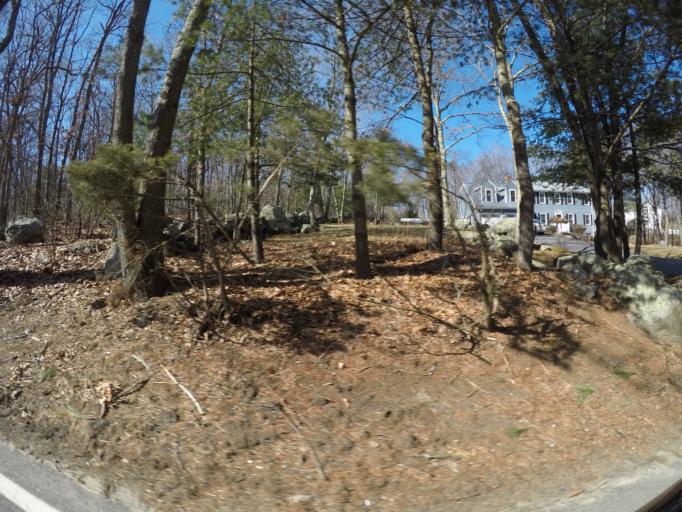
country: US
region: Massachusetts
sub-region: Norfolk County
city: Stoughton
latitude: 42.0982
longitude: -71.1328
